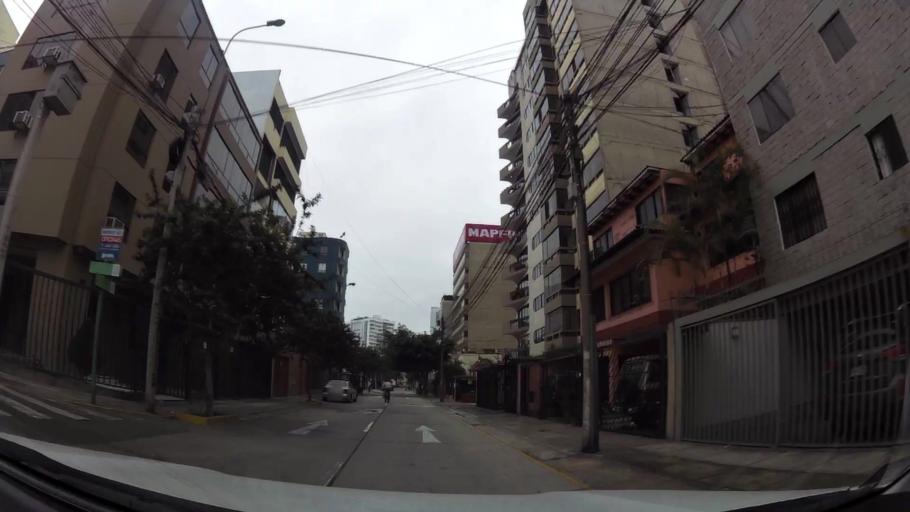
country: PE
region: Lima
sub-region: Lima
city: Surco
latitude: -12.1275
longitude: -77.0256
